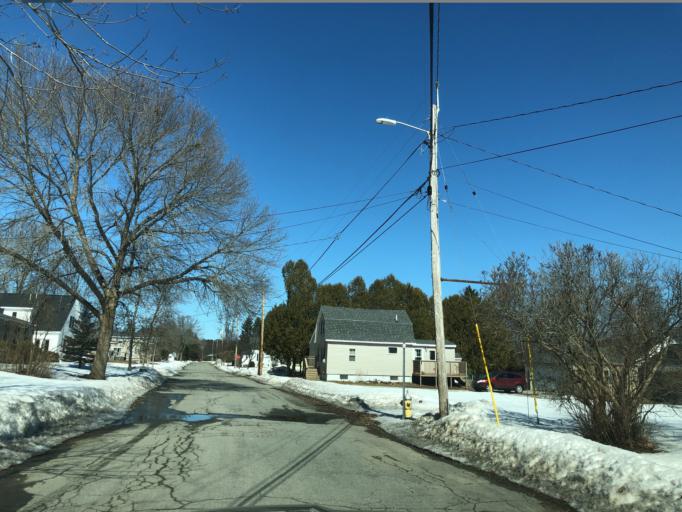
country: US
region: Maine
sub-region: Penobscot County
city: Brewer
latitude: 44.8174
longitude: -68.7541
